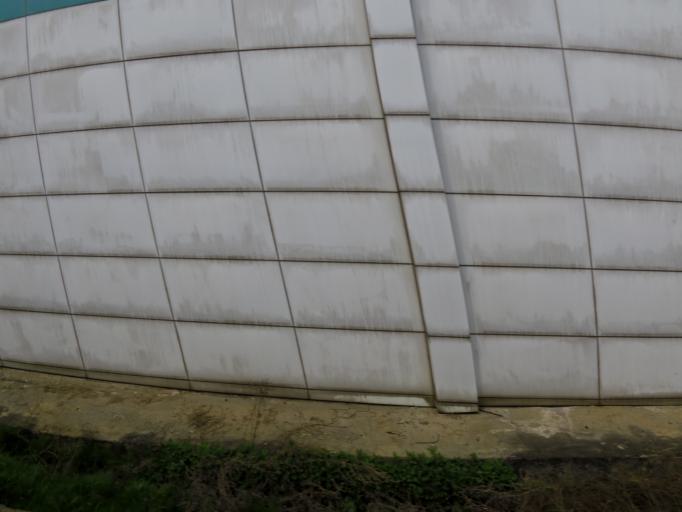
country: KR
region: Gyeonggi-do
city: Kwangmyong
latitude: 37.5131
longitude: 126.9258
